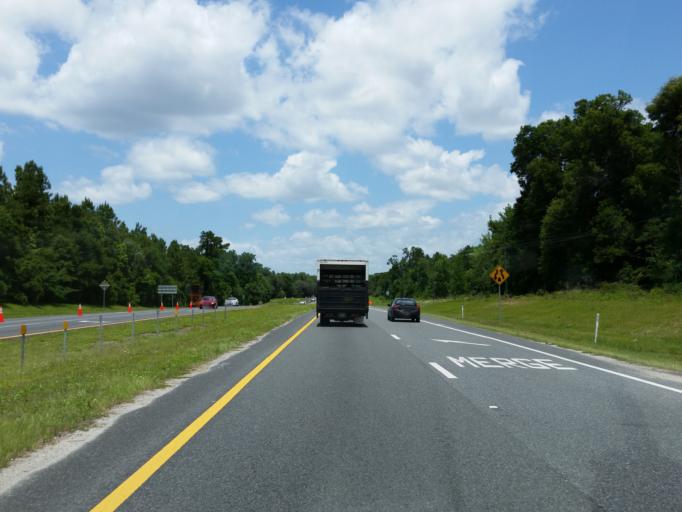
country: US
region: Florida
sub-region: Marion County
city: Belleview
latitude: 28.9829
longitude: -82.0412
